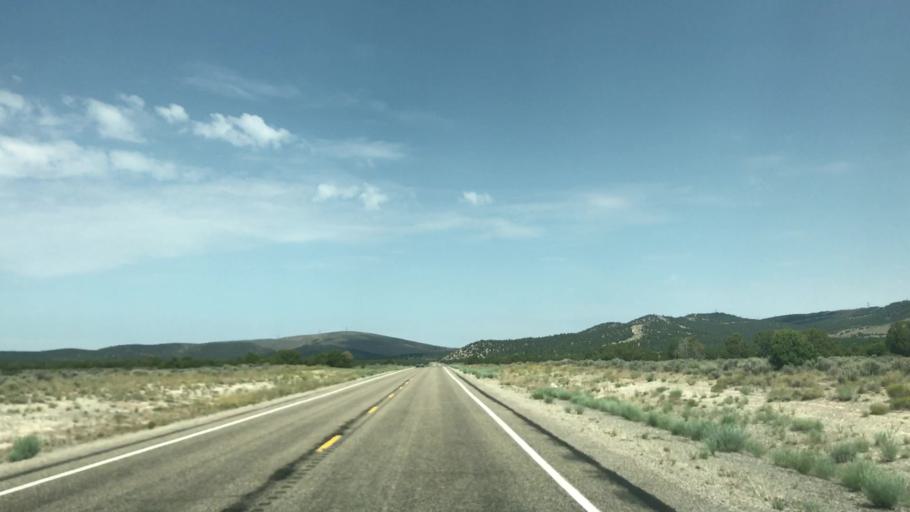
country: US
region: Nevada
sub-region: White Pine County
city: Ely
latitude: 39.3688
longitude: -115.0554
